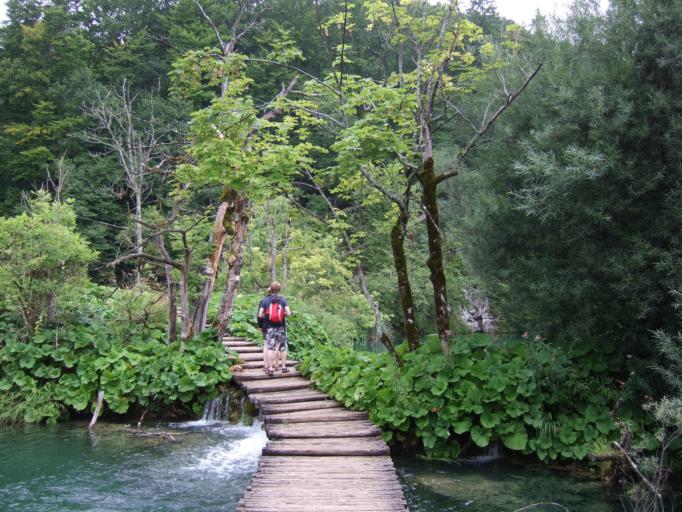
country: HR
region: Licko-Senjska
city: Jezerce
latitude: 44.8801
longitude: 15.6142
